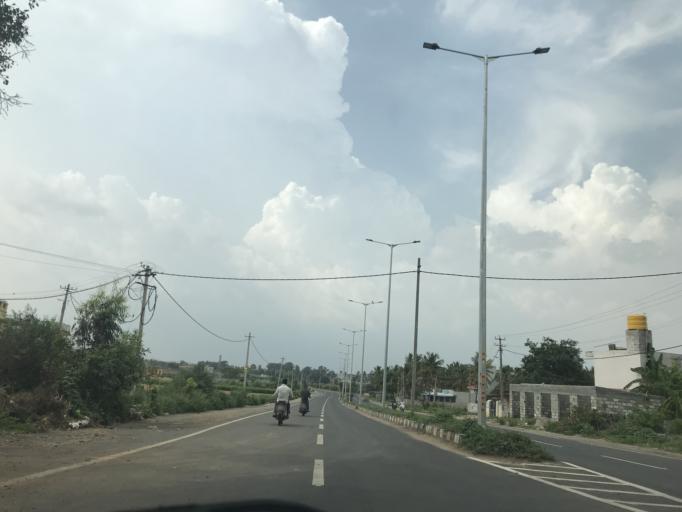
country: IN
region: Karnataka
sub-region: Bangalore Rural
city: Devanhalli
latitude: 13.1737
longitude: 77.6914
